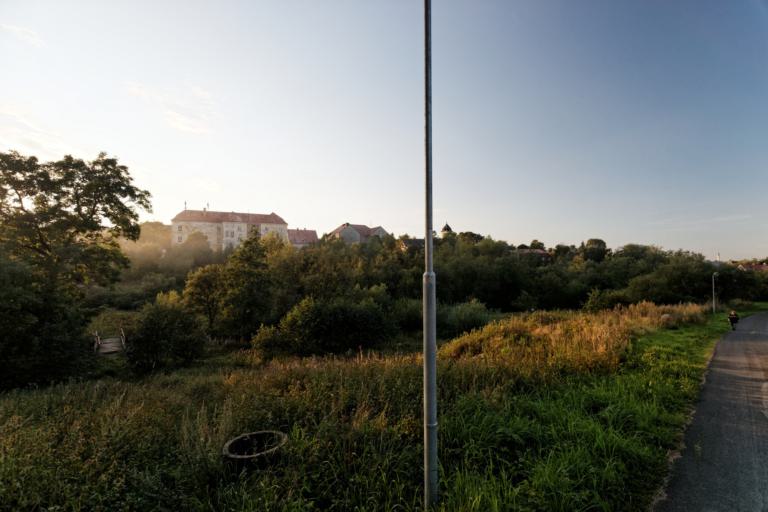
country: CZ
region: Ustecky
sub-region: Okres Chomutov
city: Kovarska
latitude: 50.4376
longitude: 13.0561
